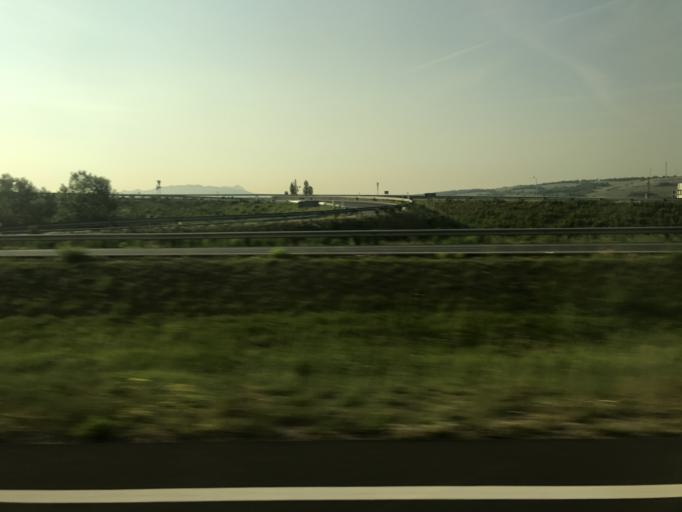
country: ES
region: Basque Country
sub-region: Provincia de Alava
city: Arminon
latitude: 42.7091
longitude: -2.9088
